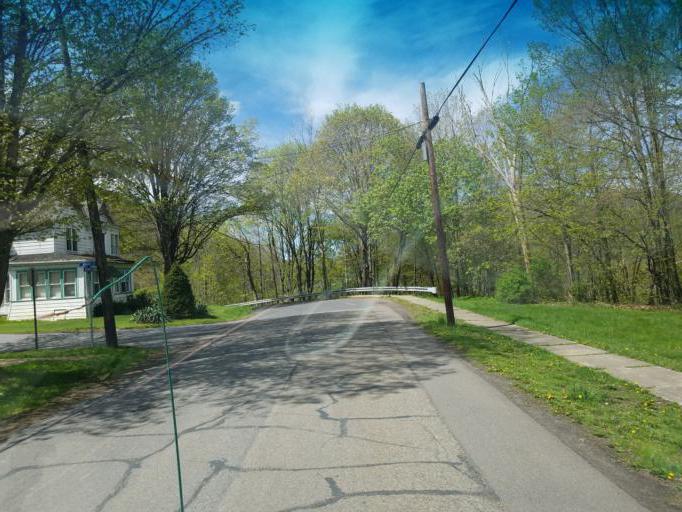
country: US
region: Pennsylvania
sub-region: Potter County
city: Galeton
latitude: 41.7337
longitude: -77.6393
